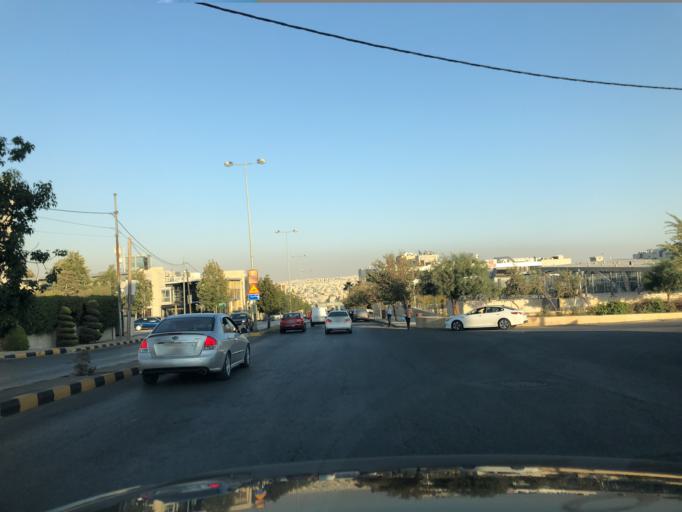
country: JO
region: Amman
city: Al Bunayyat ash Shamaliyah
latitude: 31.9416
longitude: 35.8829
